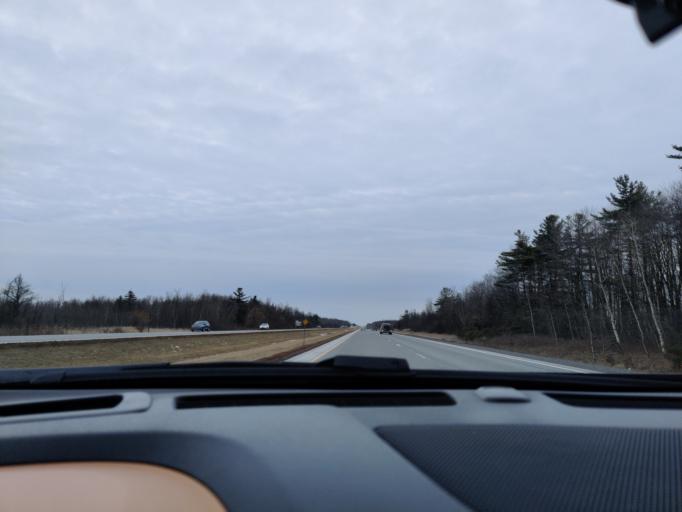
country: US
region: New York
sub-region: St. Lawrence County
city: Ogdensburg
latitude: 44.8497
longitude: -75.3431
